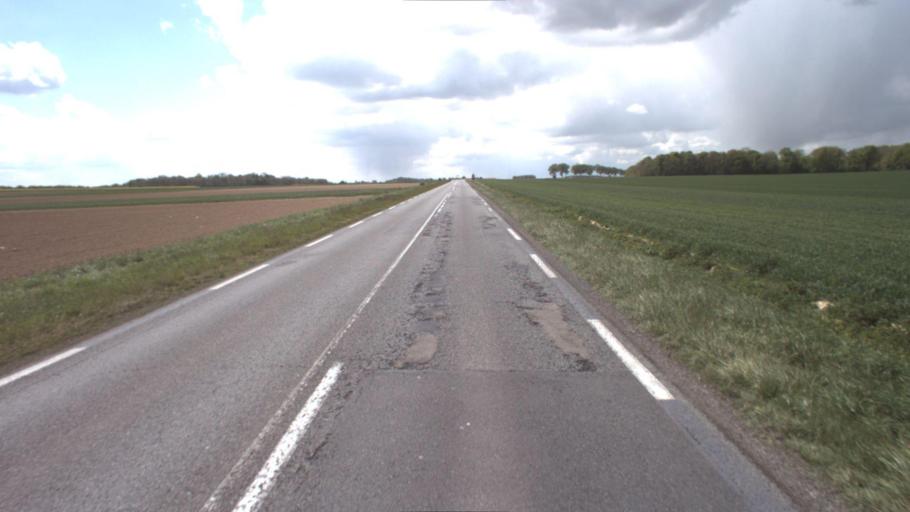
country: FR
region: Ile-de-France
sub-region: Departement de Seine-et-Marne
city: Choisy-en-Brie
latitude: 48.6939
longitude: 3.2246
